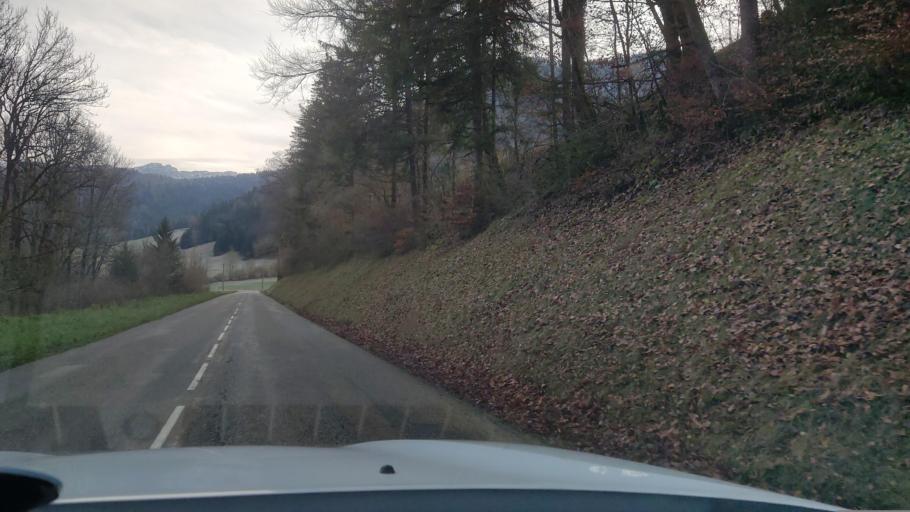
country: FR
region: Rhone-Alpes
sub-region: Departement de la Haute-Savoie
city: Doussard
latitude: 45.6730
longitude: 6.1447
